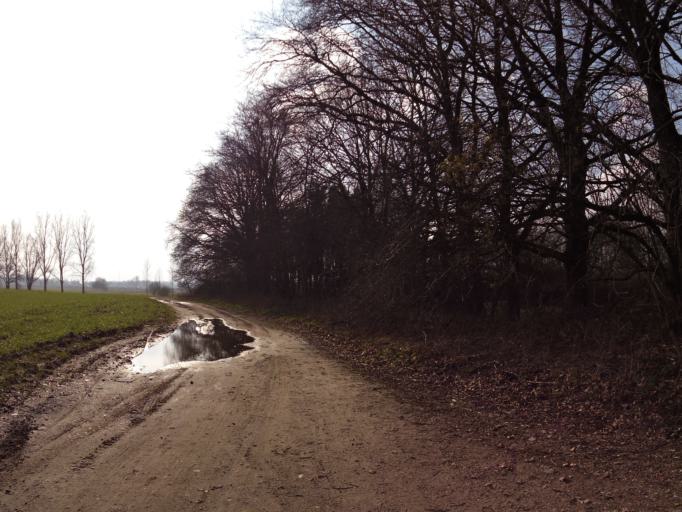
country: NL
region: North Brabant
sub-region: Gemeente Boxtel
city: Boxtel
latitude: 51.6085
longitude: 5.3361
